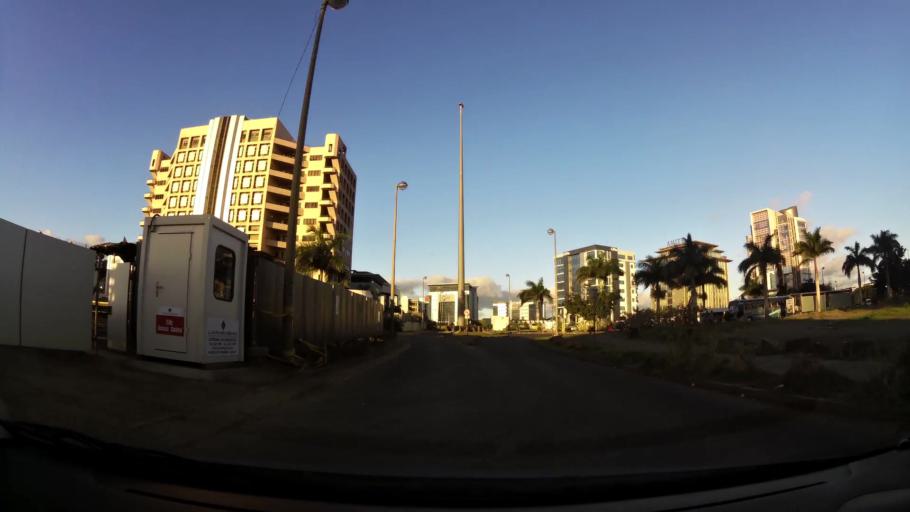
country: MU
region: Plaines Wilhems
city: Ebene
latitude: -20.2432
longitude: 57.4913
